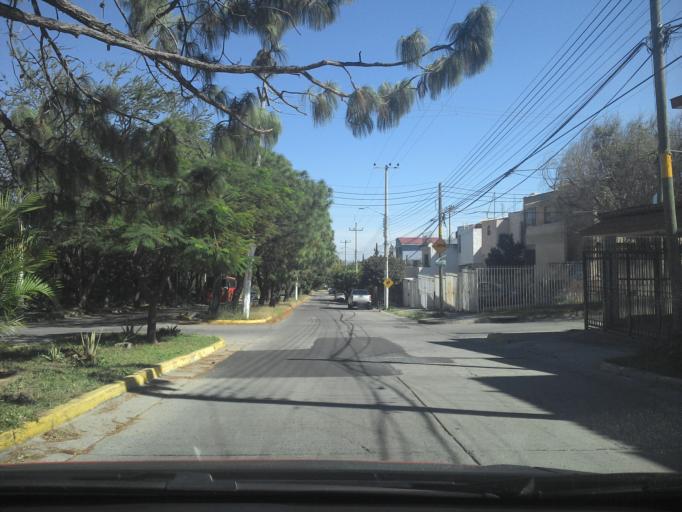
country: MX
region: Jalisco
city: Zapopan2
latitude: 20.7481
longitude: -103.4089
